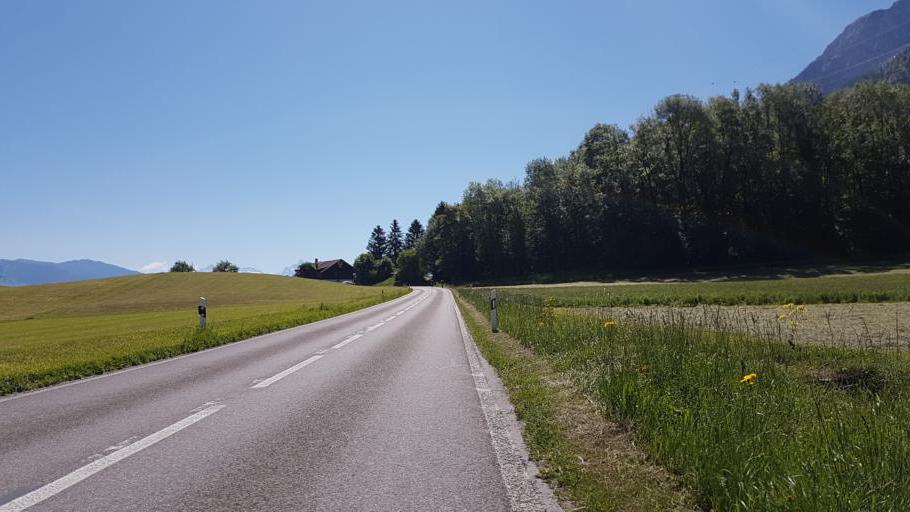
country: CH
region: Bern
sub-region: Thun District
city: Blumenstein
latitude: 46.7192
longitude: 7.5446
